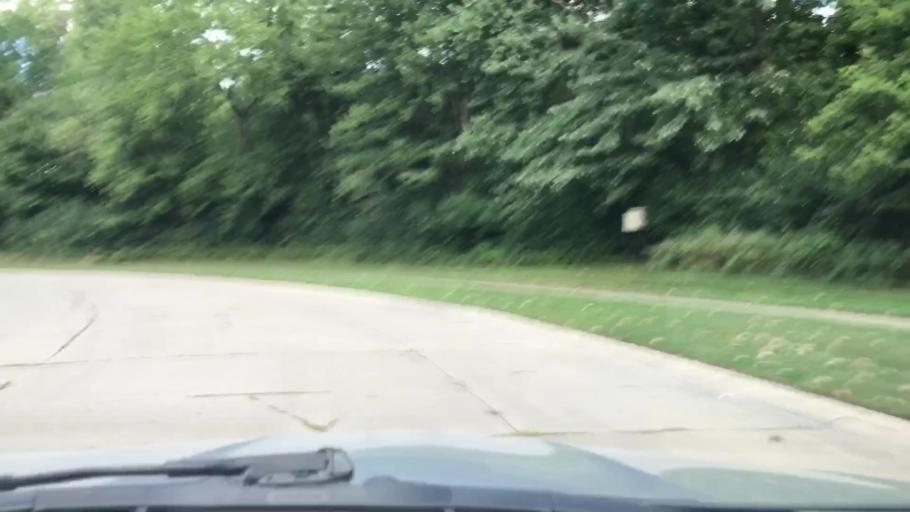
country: US
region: Michigan
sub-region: Macomb County
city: Utica
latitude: 42.6046
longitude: -83.0854
